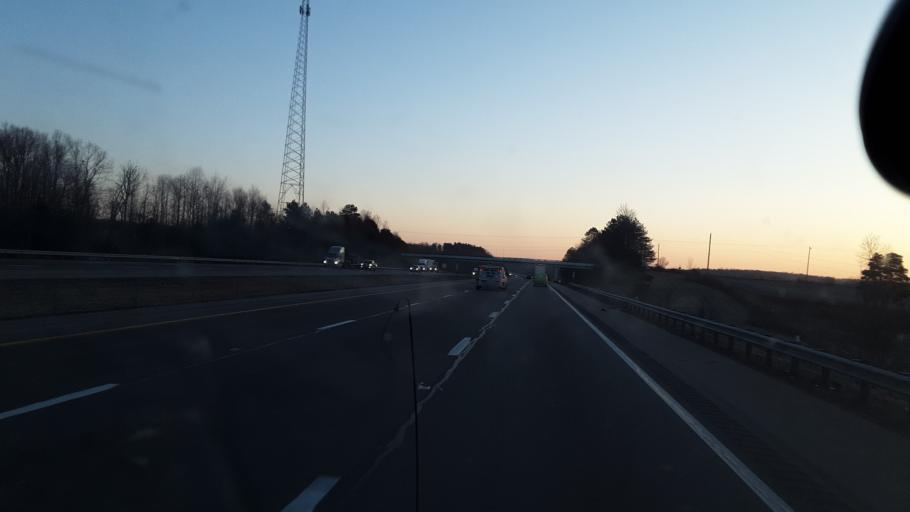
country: US
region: Ohio
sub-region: Knox County
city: Fredericktown
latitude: 40.5660
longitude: -82.6265
